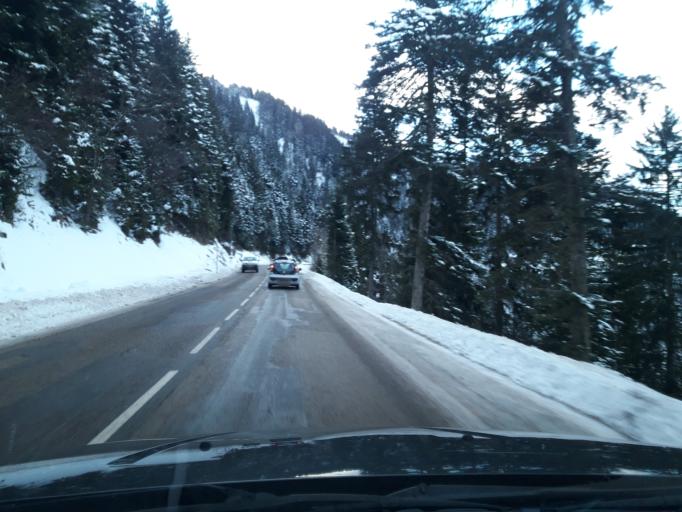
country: FR
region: Rhone-Alpes
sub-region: Departement de l'Isere
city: Revel
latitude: 45.1401
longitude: 5.8800
